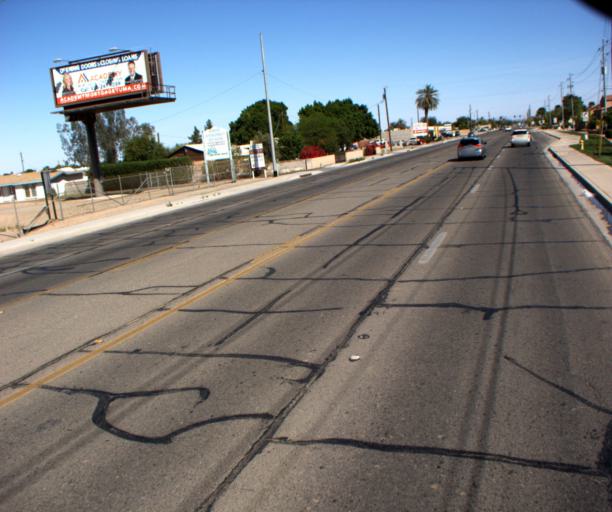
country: US
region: Arizona
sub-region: Yuma County
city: Yuma
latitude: 32.6736
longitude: -114.6501
